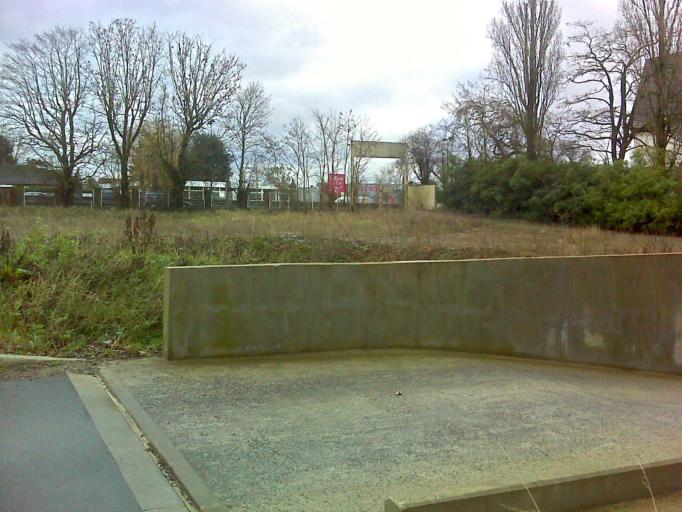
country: FR
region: Nord-Pas-de-Calais
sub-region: Departement du Nord
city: Wattignies
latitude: 50.5890
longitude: 3.0500
